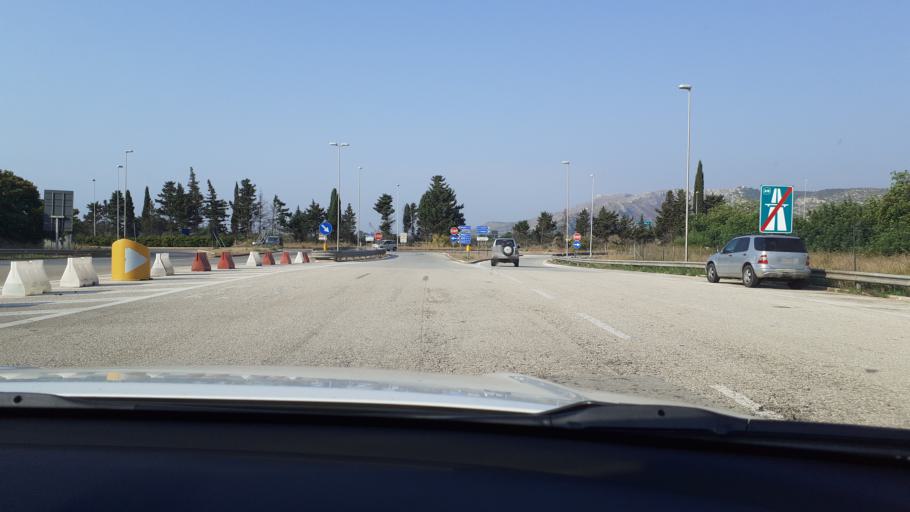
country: IT
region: Sicily
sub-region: Provincia di Siracusa
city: Cassibile
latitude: 36.9731
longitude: 15.1914
